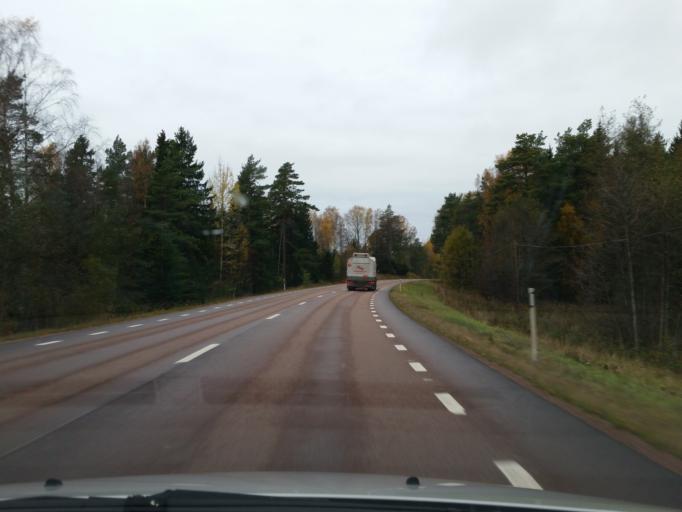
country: AX
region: Alands landsbygd
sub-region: Lemland
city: Lemland
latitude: 60.0638
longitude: 20.0488
